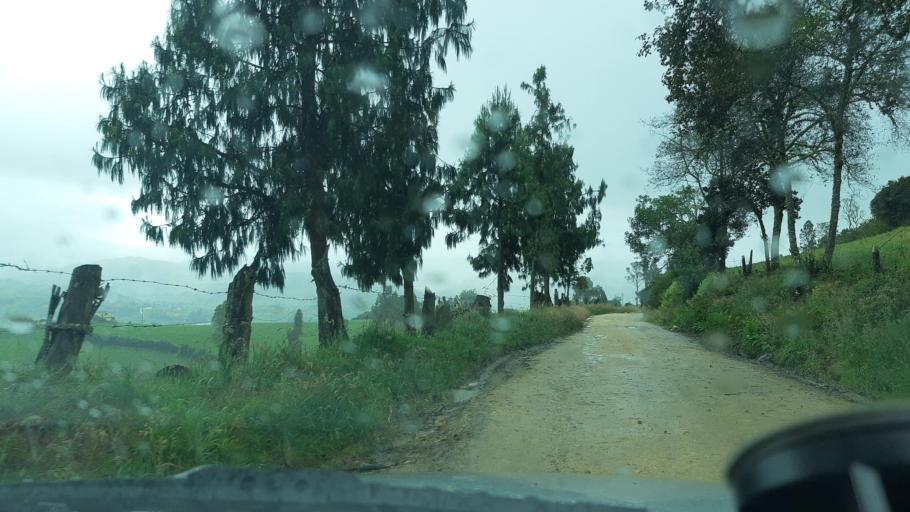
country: CO
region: Cundinamarca
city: Villapinzon
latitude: 5.2100
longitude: -73.5684
